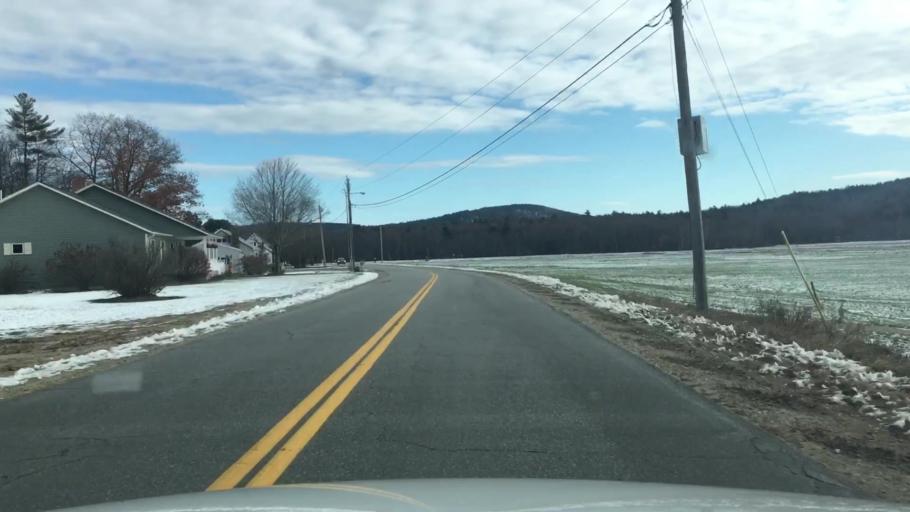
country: US
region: Maine
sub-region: Oxford County
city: Canton
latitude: 44.4689
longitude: -70.3046
